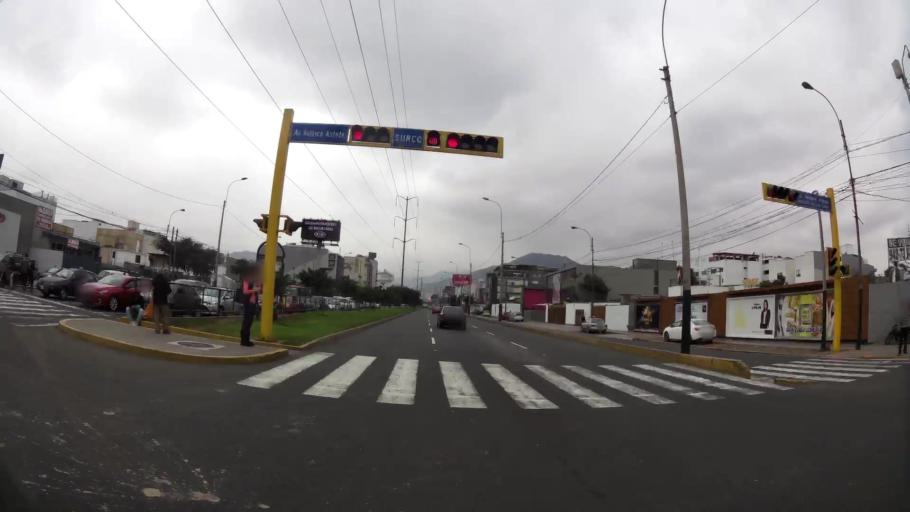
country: PE
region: Lima
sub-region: Lima
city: San Luis
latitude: -12.1107
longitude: -76.9845
